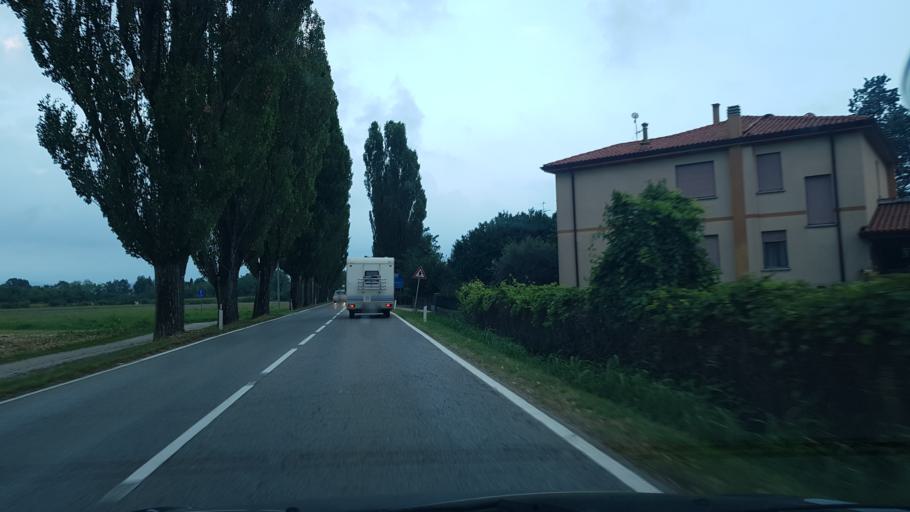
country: IT
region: Friuli Venezia Giulia
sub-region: Provincia di Gorizia
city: Romans d'Isonzo
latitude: 45.8959
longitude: 13.4259
